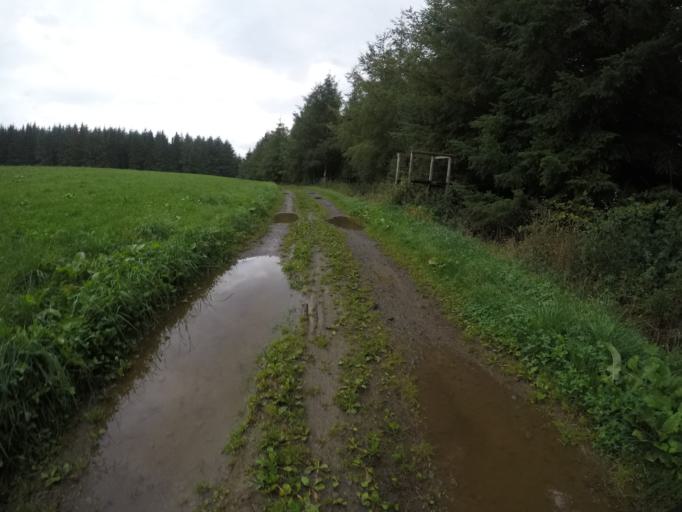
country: BE
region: Wallonia
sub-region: Province du Luxembourg
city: Fauvillers
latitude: 49.8686
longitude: 5.6875
